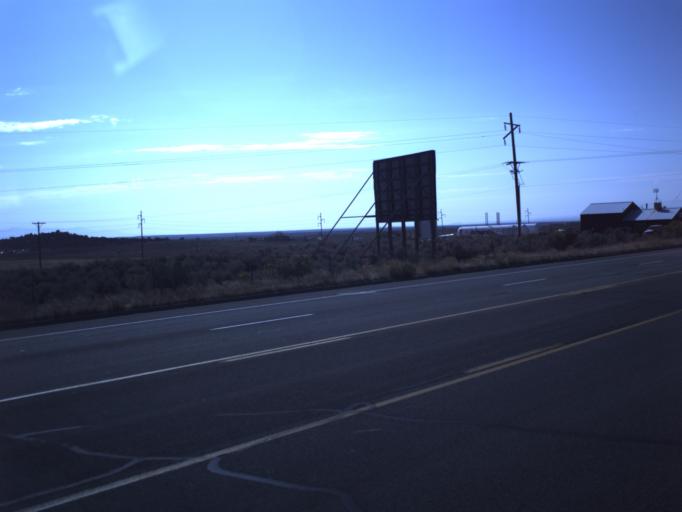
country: US
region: Utah
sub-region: San Juan County
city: Blanding
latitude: 37.6002
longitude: -109.4787
